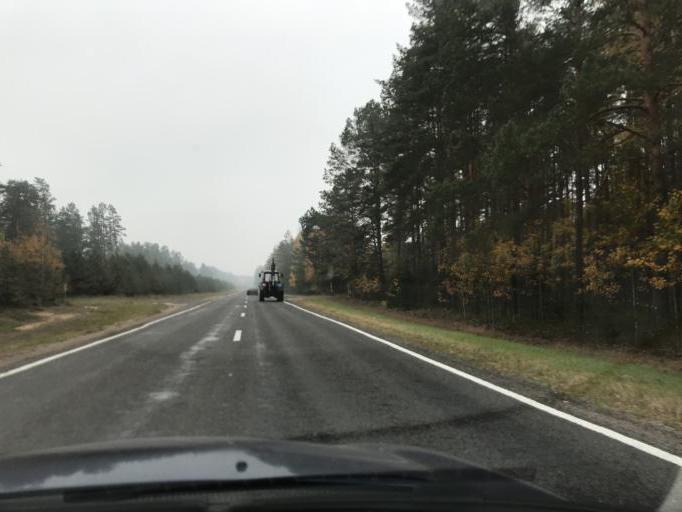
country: LT
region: Alytaus apskritis
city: Druskininkai
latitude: 53.8956
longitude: 23.9132
